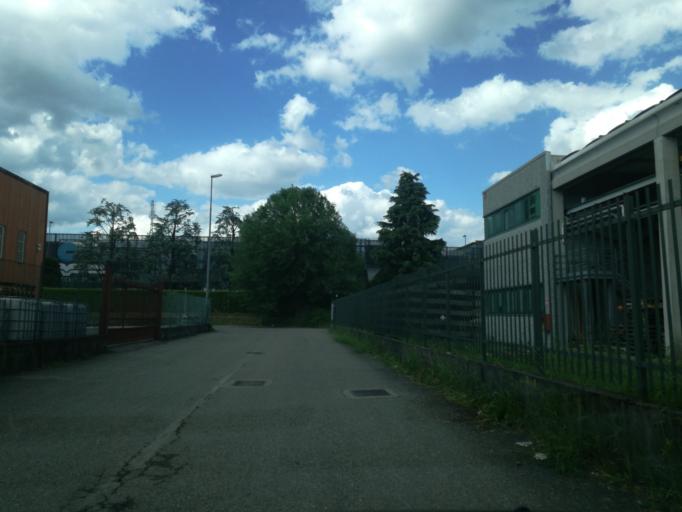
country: IT
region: Lombardy
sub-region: Provincia di Lecco
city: Verderio Inferiore
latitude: 45.6705
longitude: 9.4245
